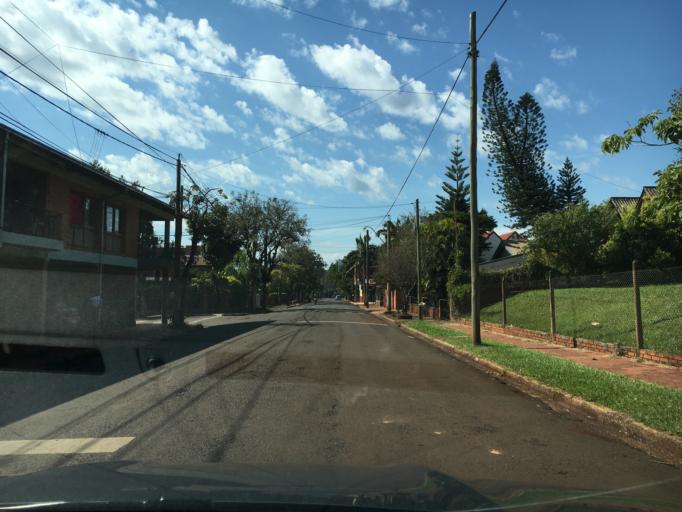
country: AR
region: Misiones
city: Puerto Rico
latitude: -26.8166
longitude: -55.0252
